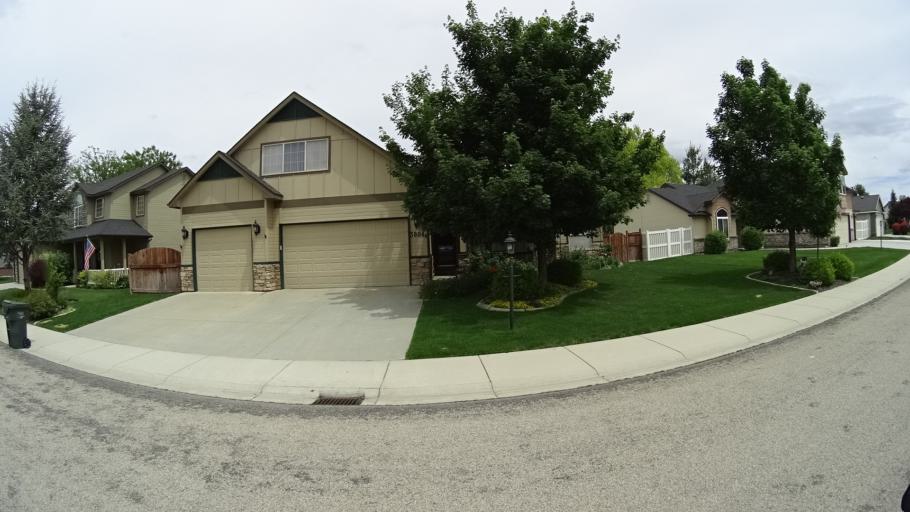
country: US
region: Idaho
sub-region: Ada County
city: Meridian
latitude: 43.6393
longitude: -116.3988
